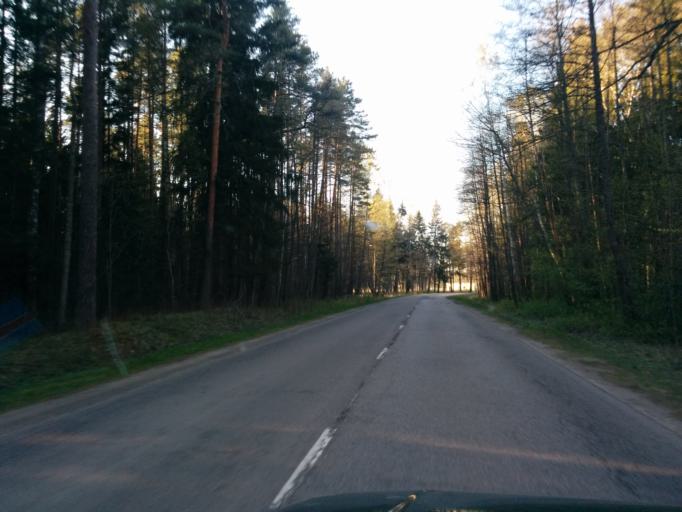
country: LV
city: Tireli
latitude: 56.9364
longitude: 23.4862
